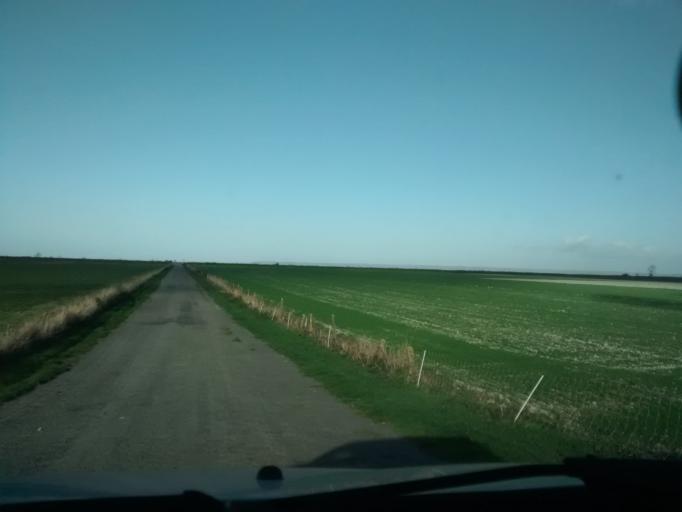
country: FR
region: Brittany
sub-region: Departement d'Ille-et-Vilaine
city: Roz-sur-Couesnon
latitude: 48.6164
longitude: -1.6045
